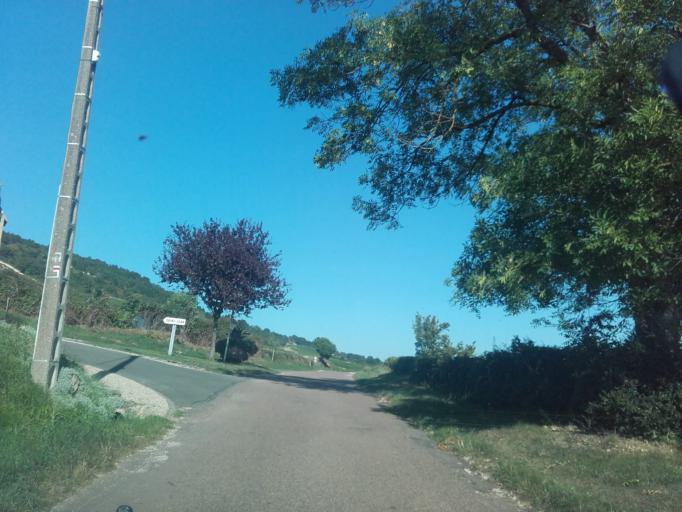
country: FR
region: Bourgogne
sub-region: Departement de la Cote-d'Or
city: Nolay
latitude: 46.9150
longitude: 4.6845
